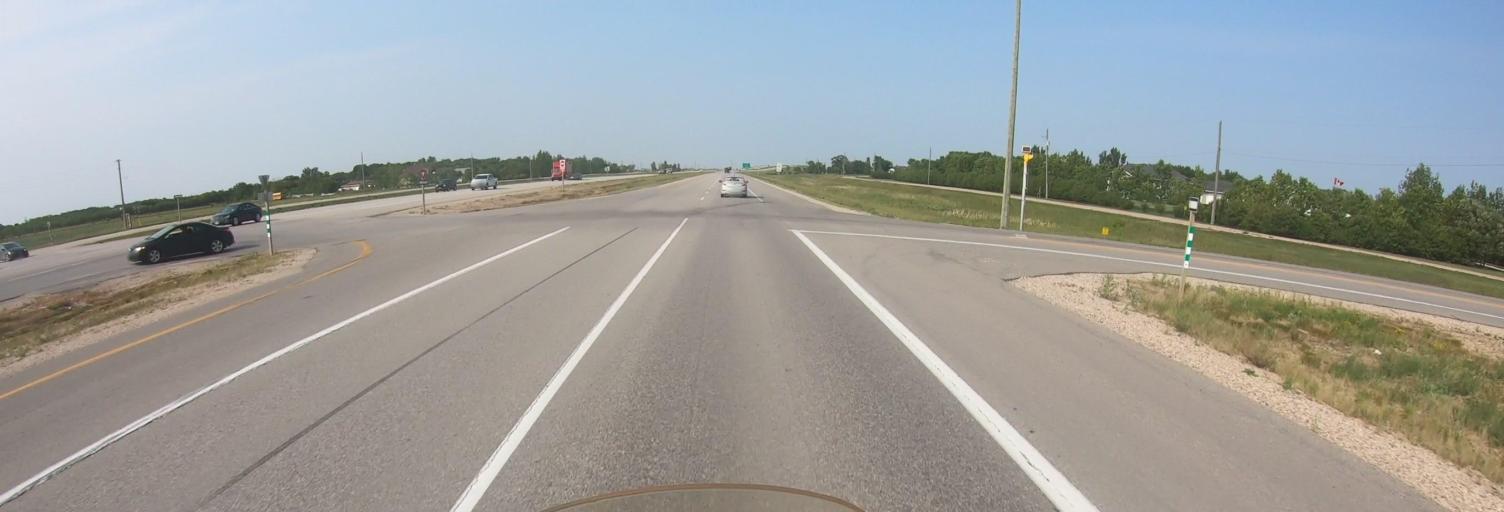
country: CA
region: Manitoba
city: Steinbach
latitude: 49.6664
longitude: -96.6673
